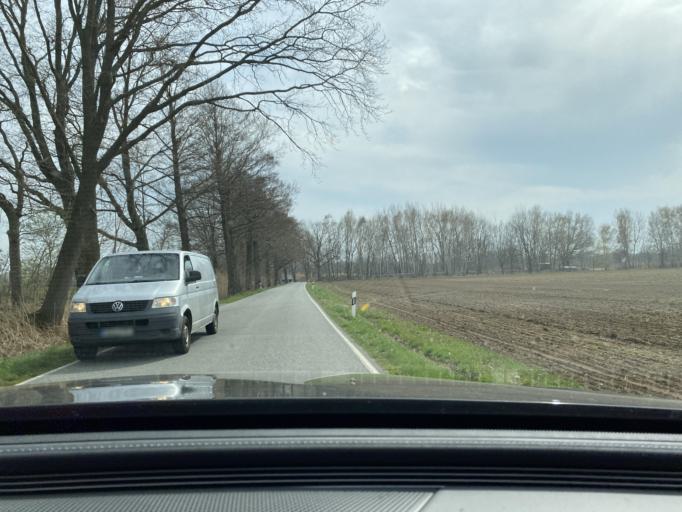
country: DE
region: Saxony
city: Konigswartha
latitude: 51.3293
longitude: 14.3029
